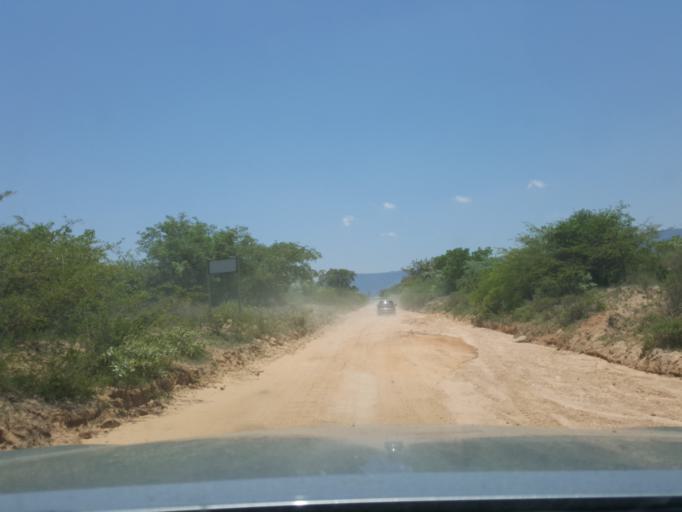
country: ZA
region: Limpopo
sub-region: Mopani District Municipality
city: Hoedspruit
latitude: -24.5778
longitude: 30.9932
